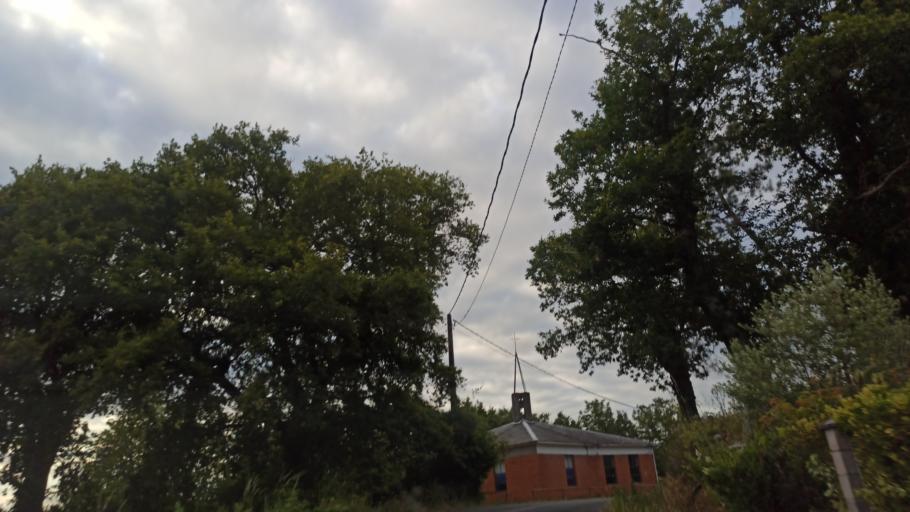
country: ES
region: Galicia
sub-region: Provincia da Coruna
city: Santiso
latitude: 42.8330
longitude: -8.1245
